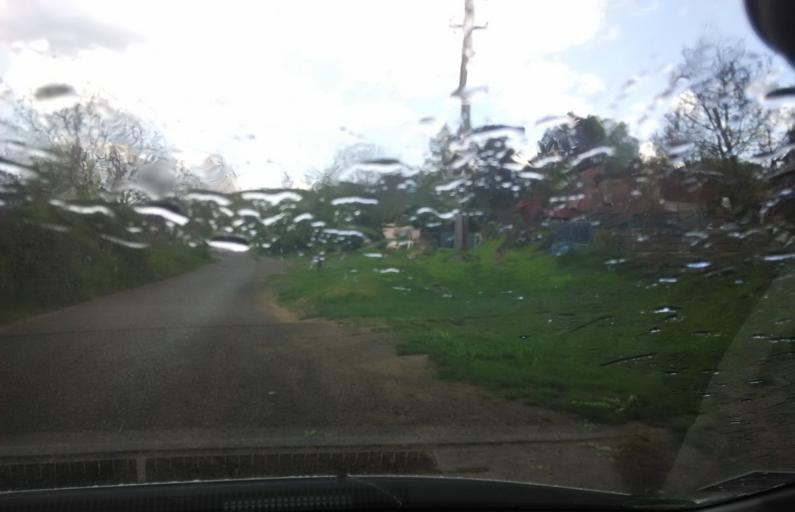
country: SK
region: Nitriansky
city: Levice
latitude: 48.2036
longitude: 18.6315
